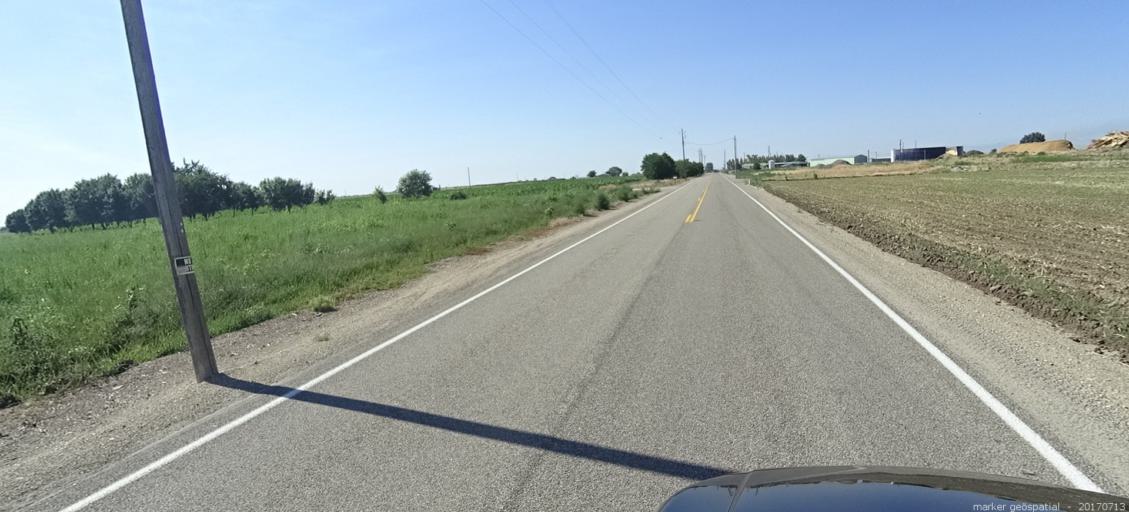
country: US
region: Idaho
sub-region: Ada County
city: Kuna
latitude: 43.5370
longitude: -116.3743
